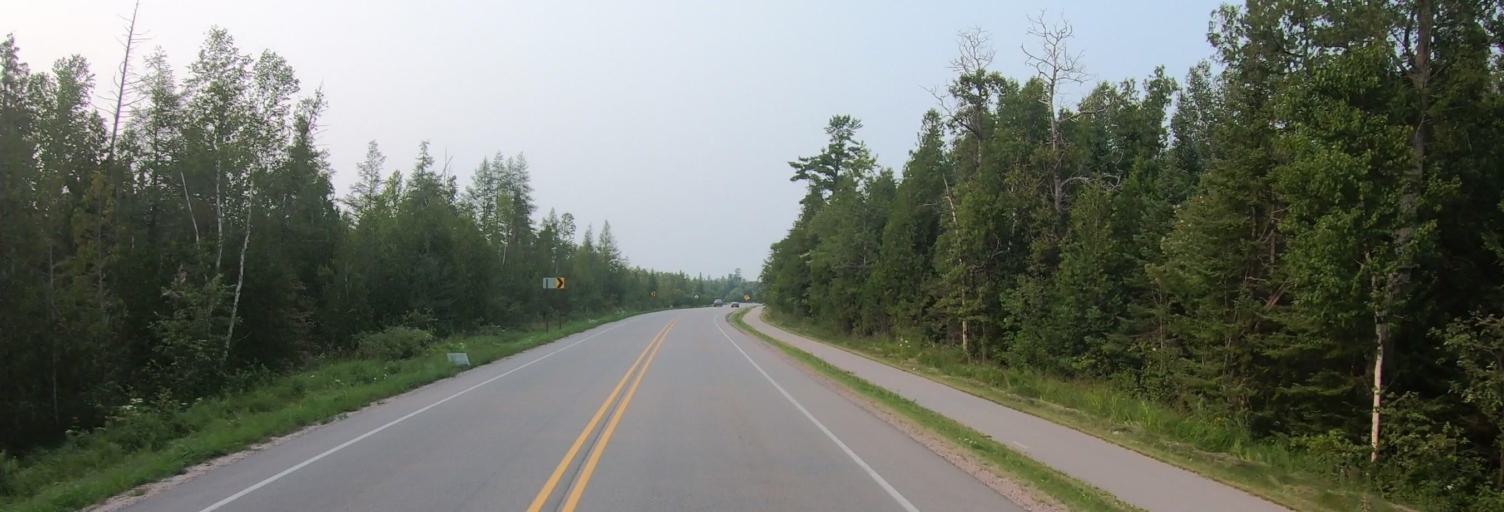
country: US
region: Michigan
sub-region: Chippewa County
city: Sault Ste. Marie
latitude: 46.4332
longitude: -84.6105
